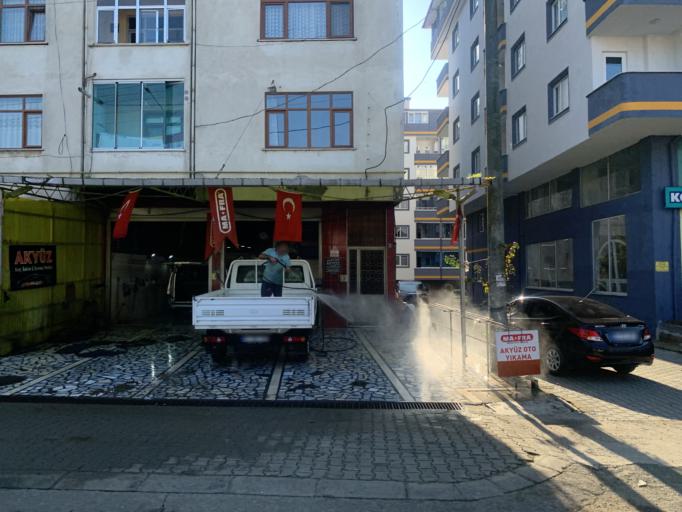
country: TR
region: Trabzon
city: Of
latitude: 40.9419
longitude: 40.2679
